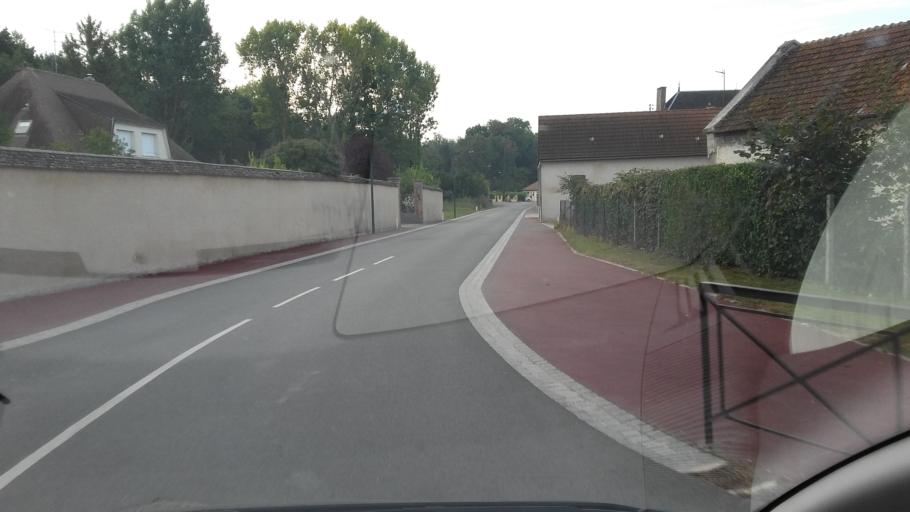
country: FR
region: Champagne-Ardenne
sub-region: Departement de la Marne
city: Connantre
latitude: 48.7294
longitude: 3.9247
